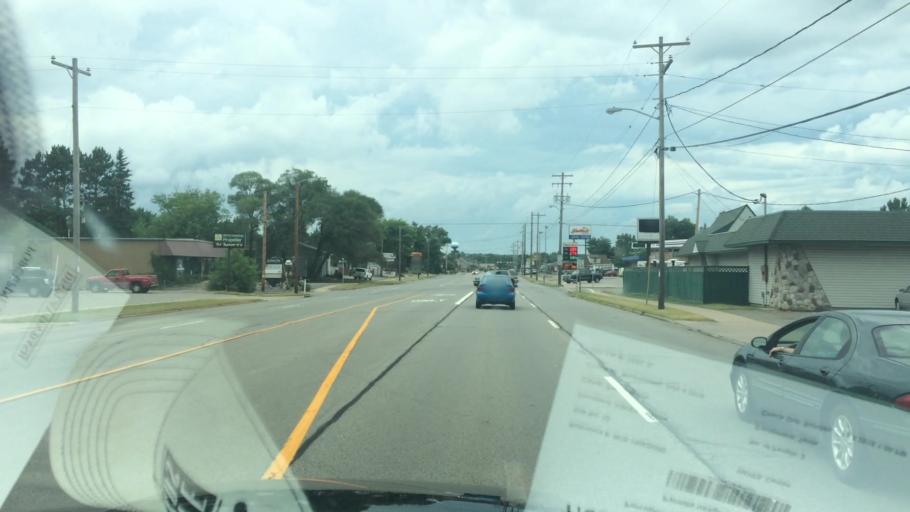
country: US
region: Wisconsin
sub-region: Marathon County
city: Schofield
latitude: 44.9047
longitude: -89.6067
